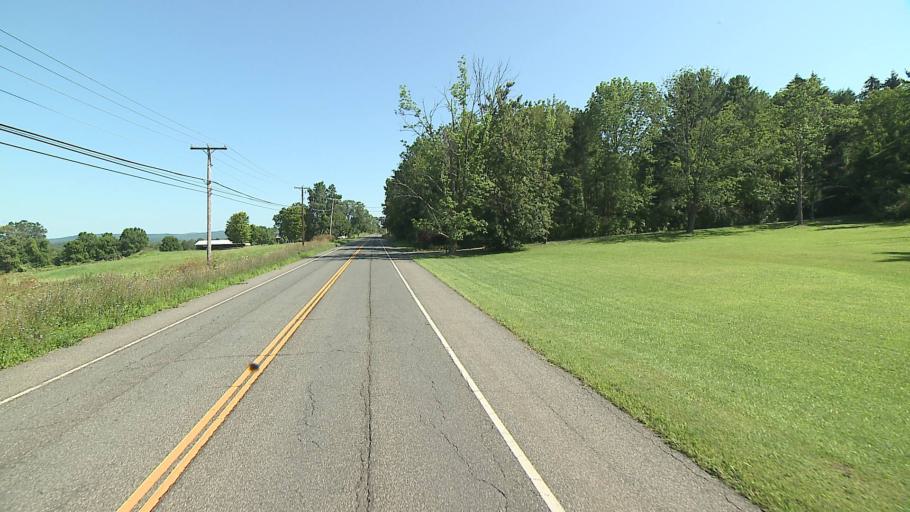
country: US
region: Connecticut
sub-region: Litchfield County
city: Canaan
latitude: 41.9142
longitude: -73.4460
